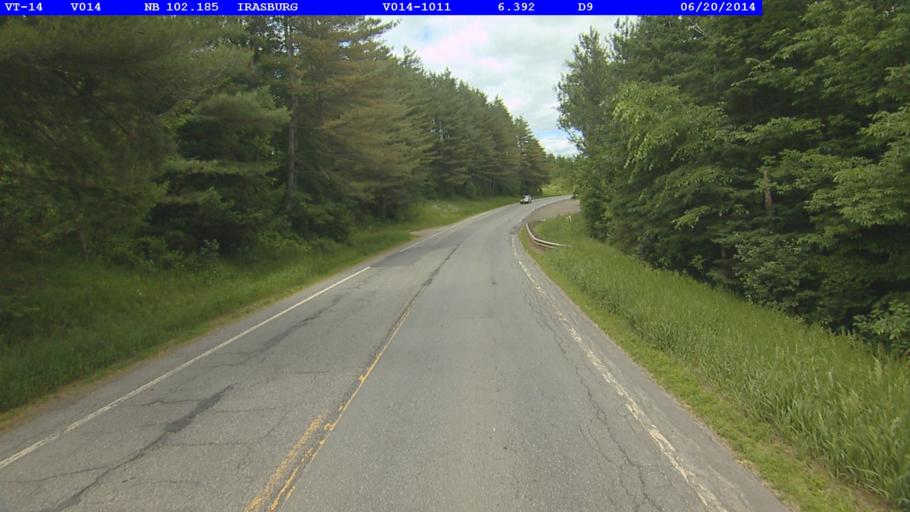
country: US
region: Vermont
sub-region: Orleans County
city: Newport
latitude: 44.8487
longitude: -72.2795
